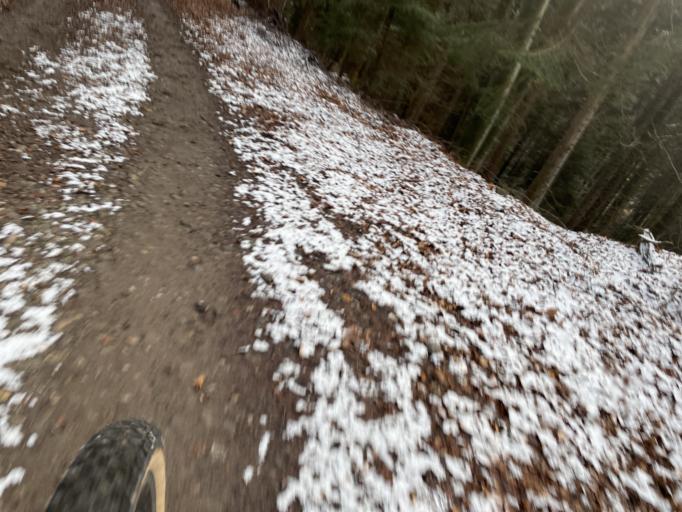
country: CH
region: Lucerne
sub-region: Entlebuch District
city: Oberdiessbach
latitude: 46.8444
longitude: 7.6046
